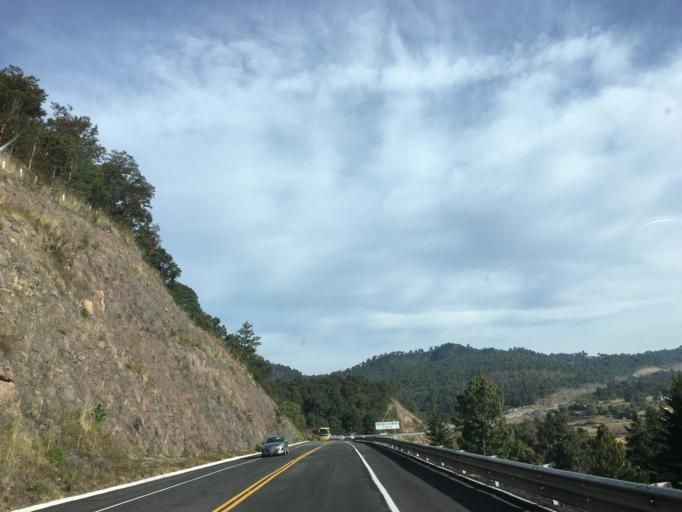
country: MX
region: Mexico
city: San Bartolo
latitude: 19.2494
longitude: -100.0672
